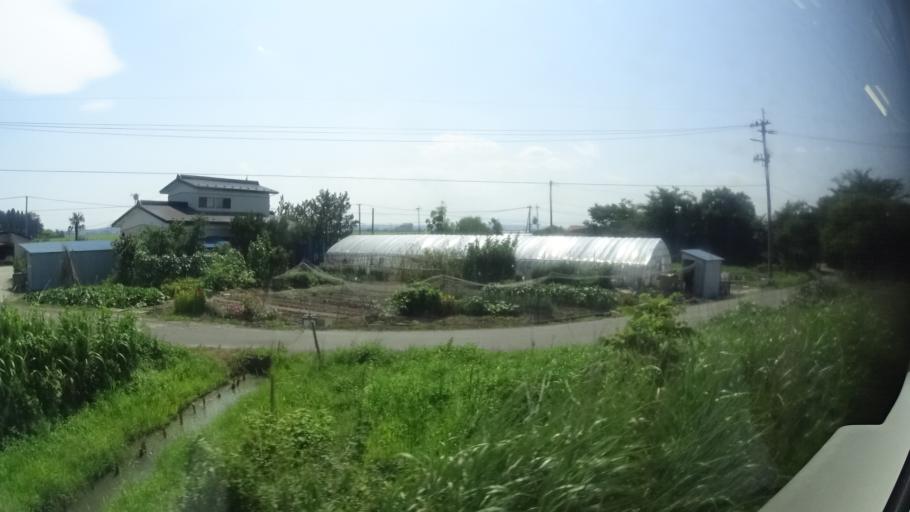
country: JP
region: Miyagi
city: Wakuya
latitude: 38.5286
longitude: 141.1464
